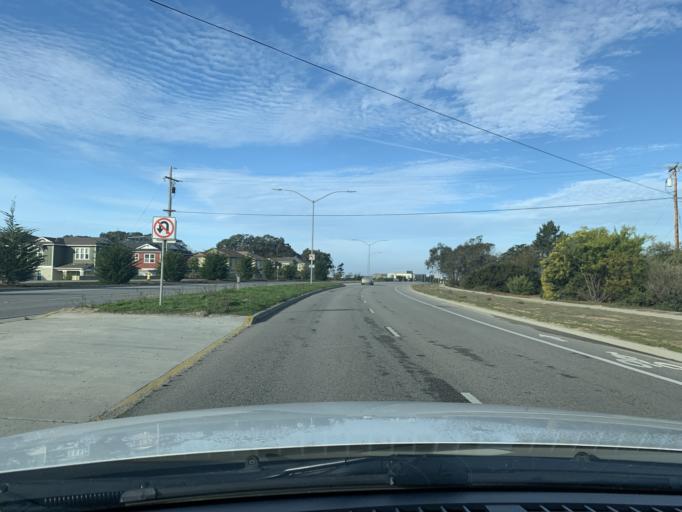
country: US
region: California
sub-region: Monterey County
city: Marina
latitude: 36.6662
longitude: -121.8024
